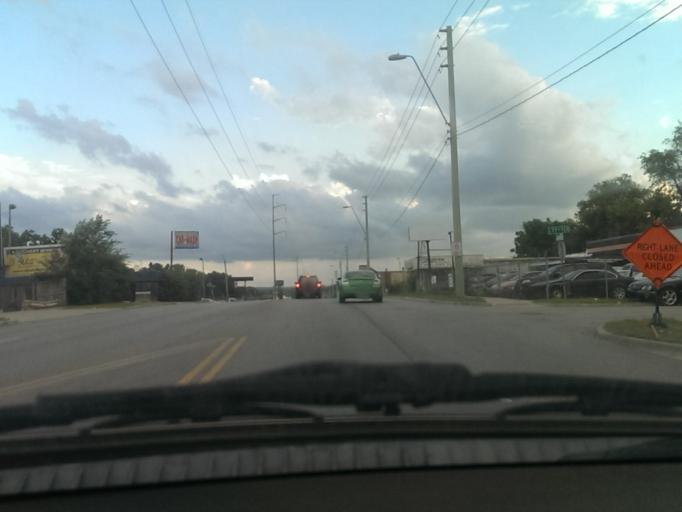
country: US
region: Kansas
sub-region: Johnson County
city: Leawood
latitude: 38.9873
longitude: -94.5760
